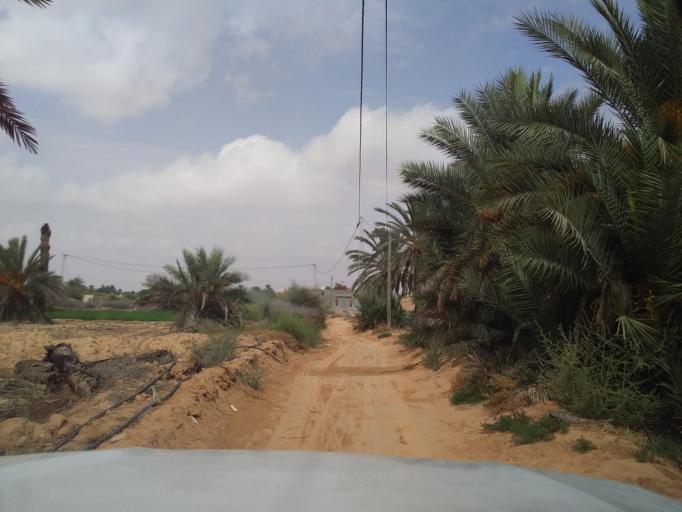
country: TN
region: Qabis
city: Gabes
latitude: 33.6257
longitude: 10.2972
